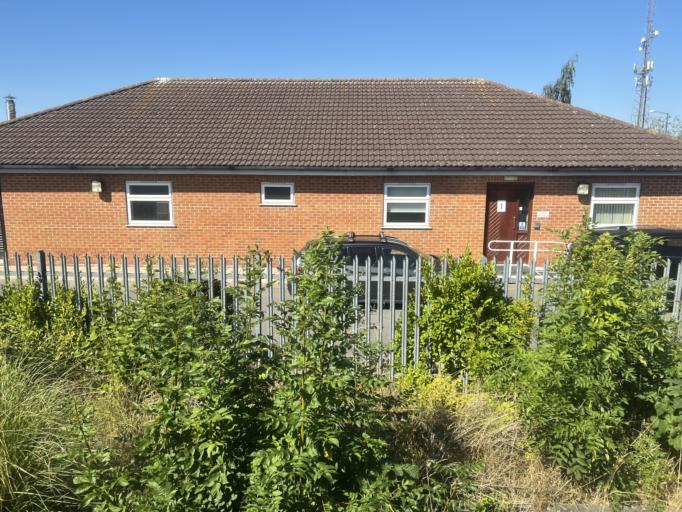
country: GB
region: England
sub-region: Lincolnshire
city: Boston
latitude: 52.9757
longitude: -0.0322
